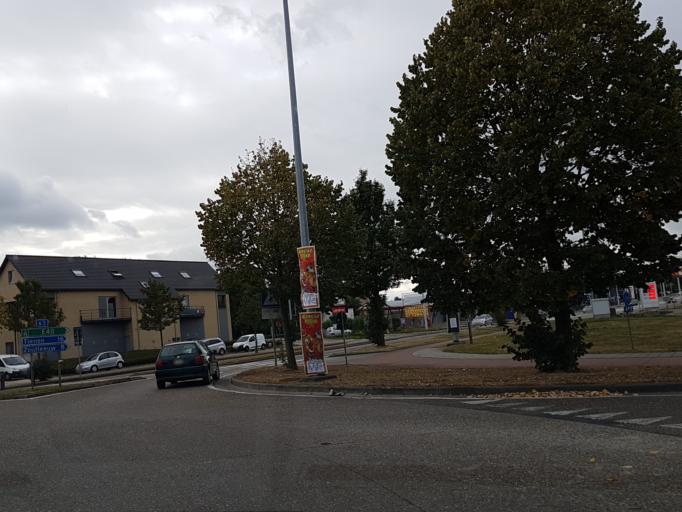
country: BE
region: Flanders
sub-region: Provincie Limburg
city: Sint-Truiden
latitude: 50.8141
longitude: 5.1618
